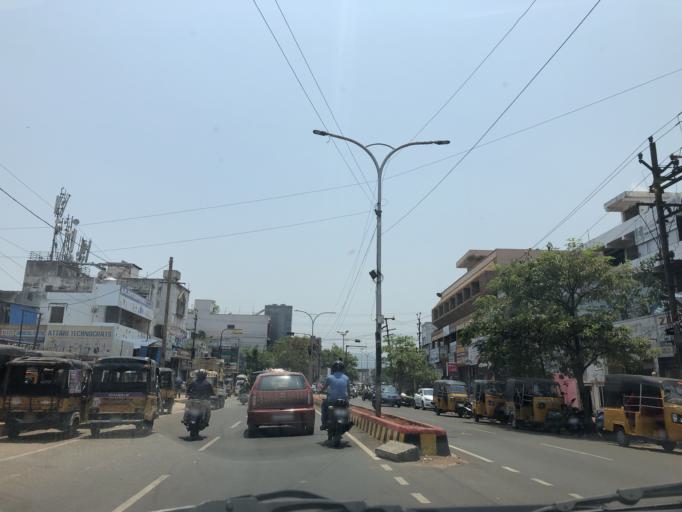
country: IN
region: Andhra Pradesh
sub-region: Vishakhapatnam
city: Yarada
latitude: 17.7104
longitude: 83.2954
